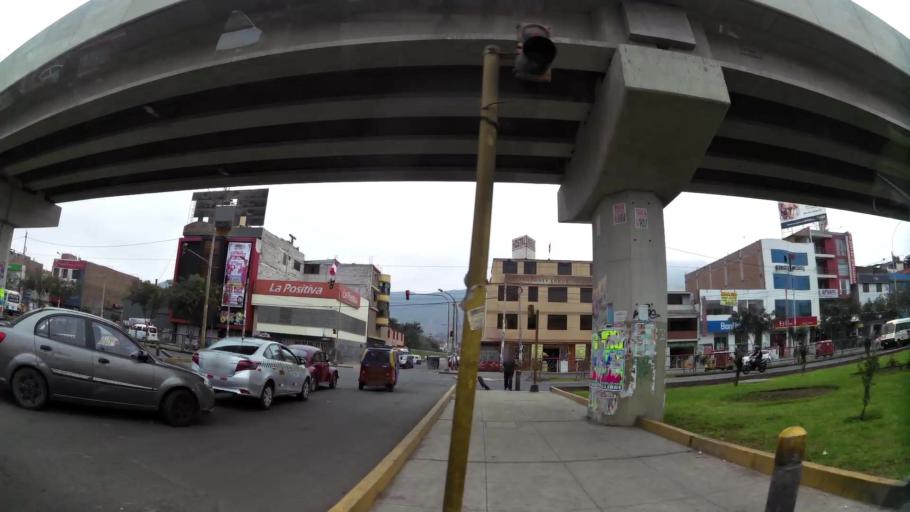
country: PE
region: Lima
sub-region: Lima
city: Independencia
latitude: -12.0013
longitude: -77.0084
